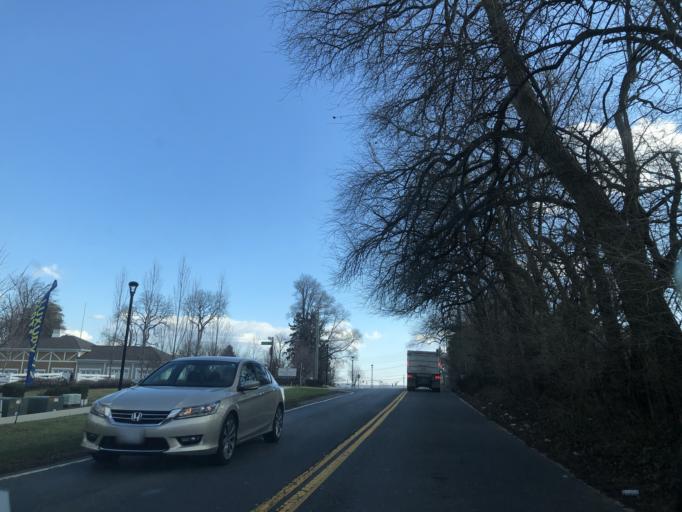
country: US
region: Maryland
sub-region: Frederick County
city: Ballenger Creek
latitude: 39.4040
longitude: -77.4424
